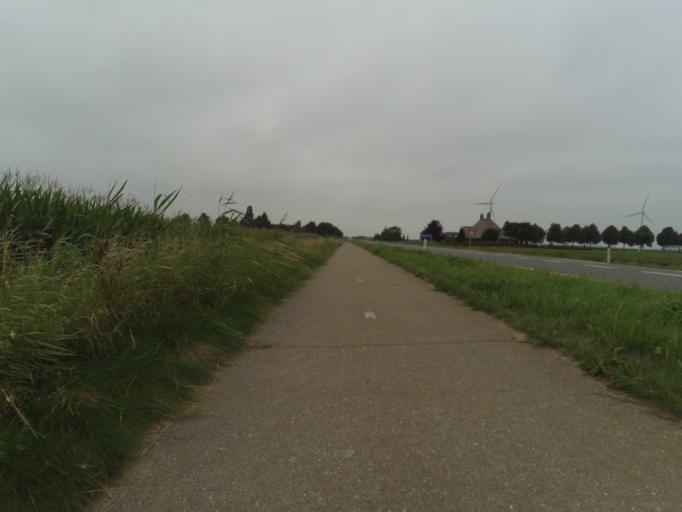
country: NL
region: Flevoland
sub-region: Gemeente Zeewolde
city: Zeewolde
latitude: 52.3691
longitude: 5.4626
